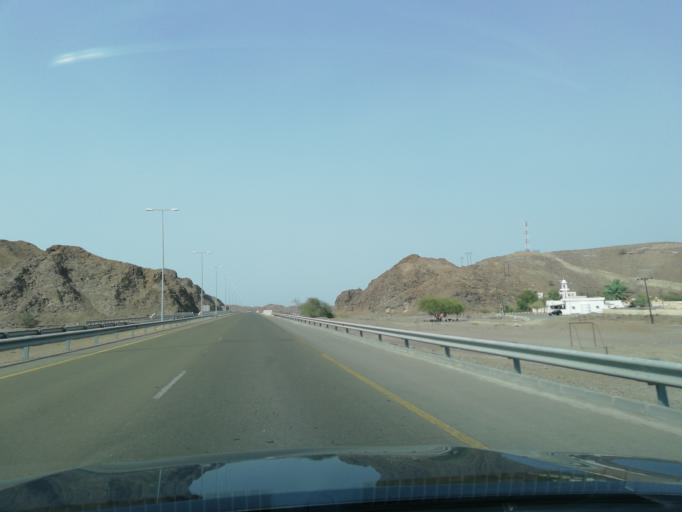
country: OM
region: Al Batinah
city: Al Liwa'
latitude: 24.3364
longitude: 56.4952
